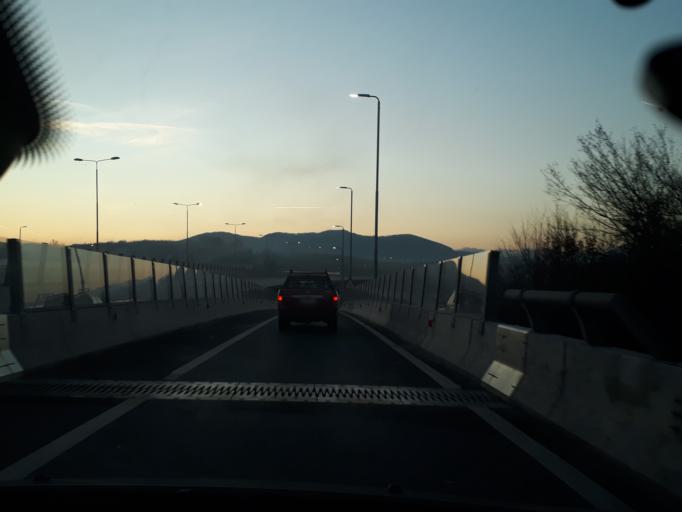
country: BA
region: Federation of Bosnia and Herzegovina
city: Hadzici
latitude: 43.8616
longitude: 18.2535
